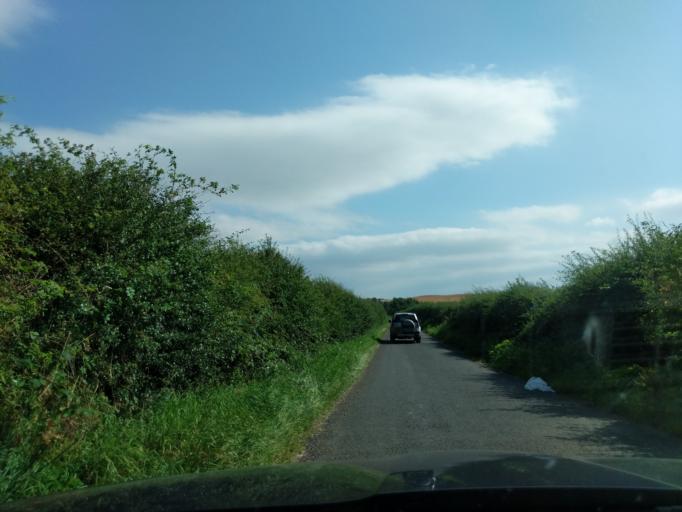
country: GB
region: England
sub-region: Northumberland
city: Ford
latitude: 55.6625
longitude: -2.1582
